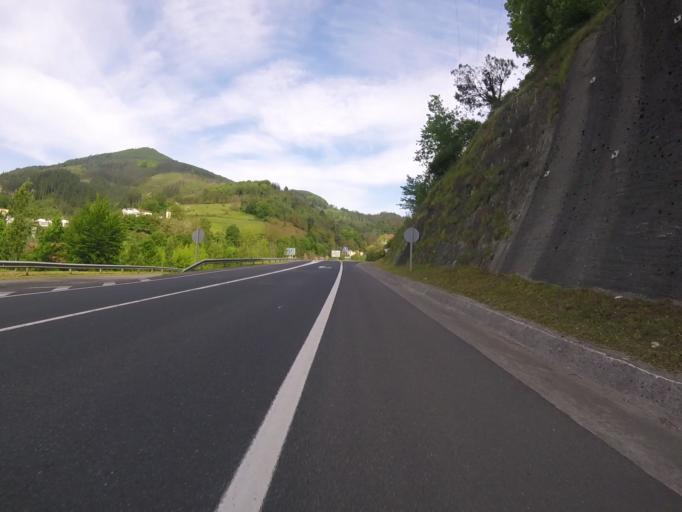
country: ES
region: Basque Country
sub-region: Provincia de Guipuzcoa
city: Urretxu
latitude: 43.0977
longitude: -2.3153
